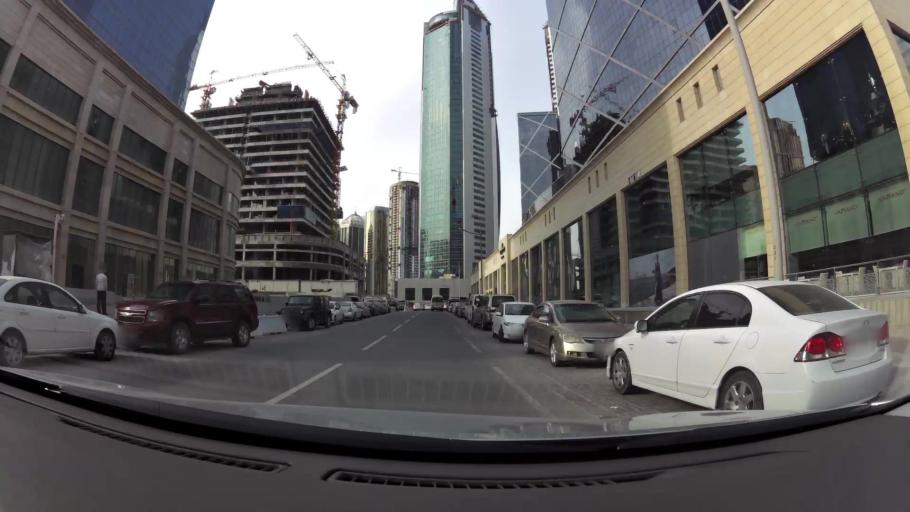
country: QA
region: Baladiyat ad Dawhah
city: Doha
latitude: 25.3220
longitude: 51.5261
